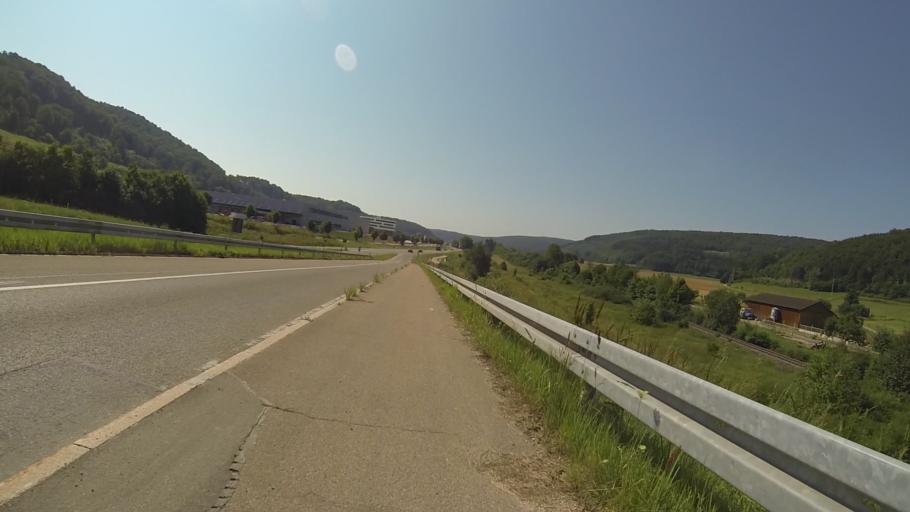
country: DE
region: Baden-Wuerttemberg
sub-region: Regierungsbezirk Stuttgart
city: Oberkochen
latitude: 48.7716
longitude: 10.1004
